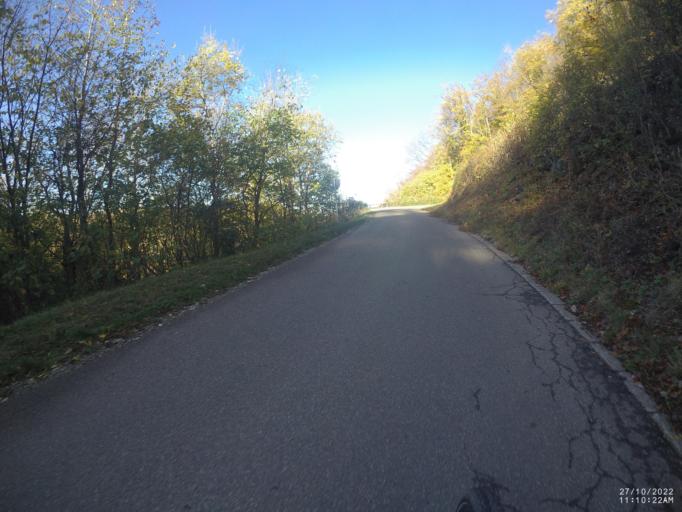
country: DE
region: Baden-Wuerttemberg
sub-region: Regierungsbezirk Stuttgart
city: Bad Ditzenbach
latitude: 48.5696
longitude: 9.6858
